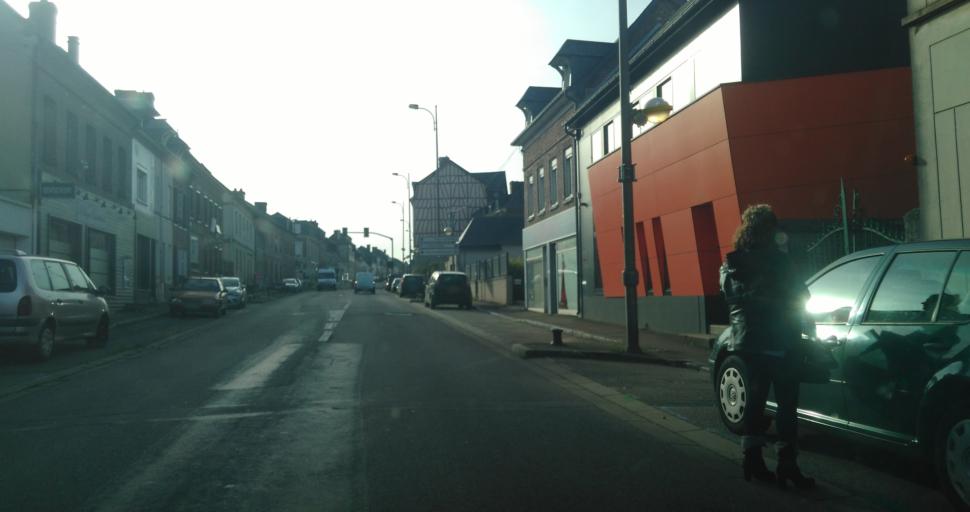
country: FR
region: Haute-Normandie
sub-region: Departement de l'Eure
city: Bourg-Achard
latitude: 49.3560
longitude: 0.8202
